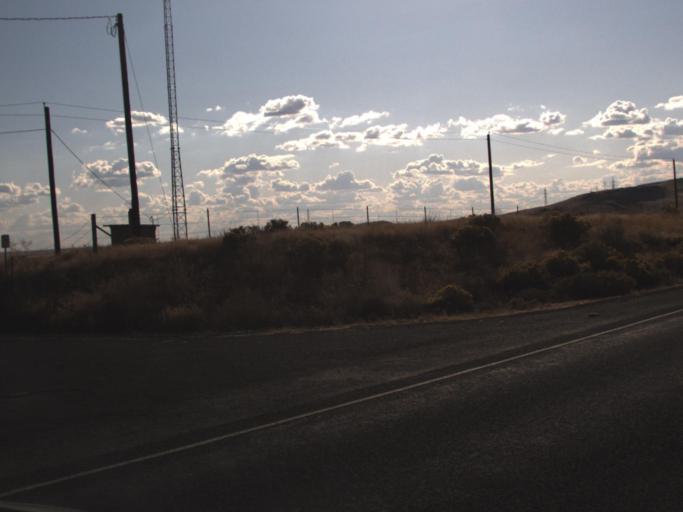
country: US
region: Oregon
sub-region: Morrow County
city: Boardman
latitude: 45.8656
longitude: -119.7903
